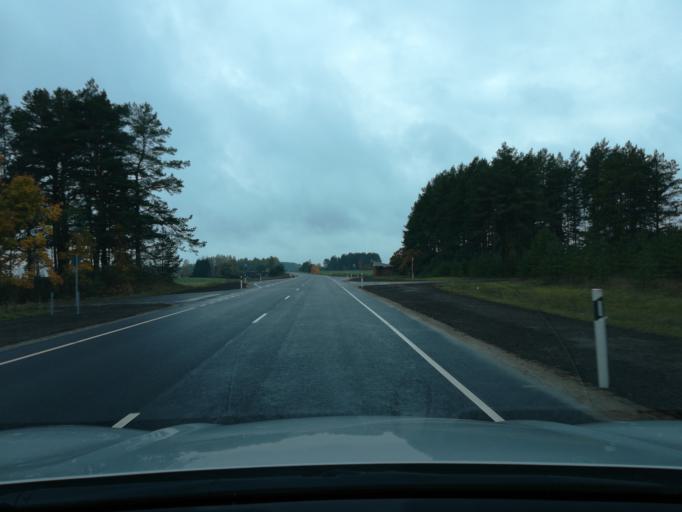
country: EE
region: Ida-Virumaa
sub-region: Johvi vald
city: Johvi
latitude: 59.1323
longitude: 27.3346
